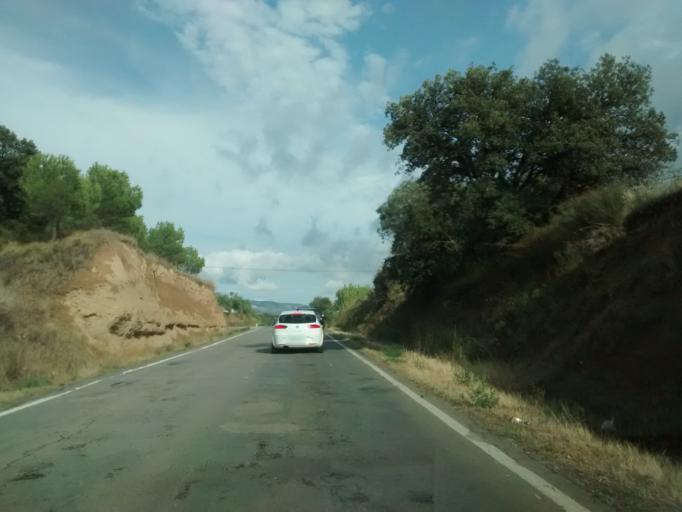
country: ES
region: Aragon
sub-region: Provincia de Huesca
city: Barbastro
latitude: 42.0445
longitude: 0.1427
